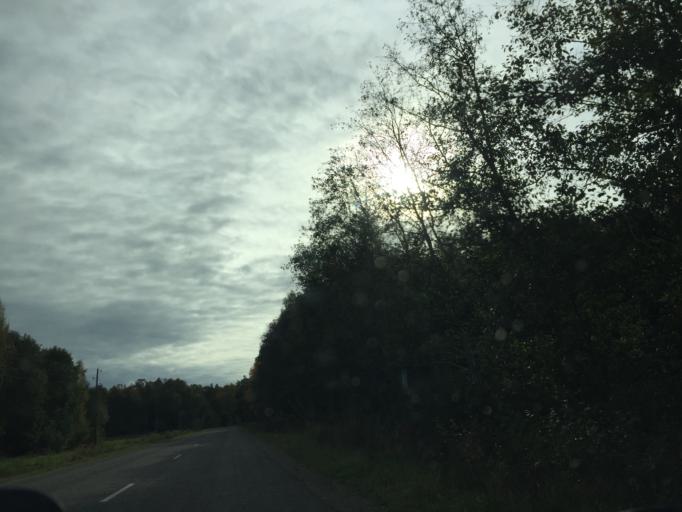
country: LV
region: Auces Novads
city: Auce
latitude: 56.5562
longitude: 23.0183
